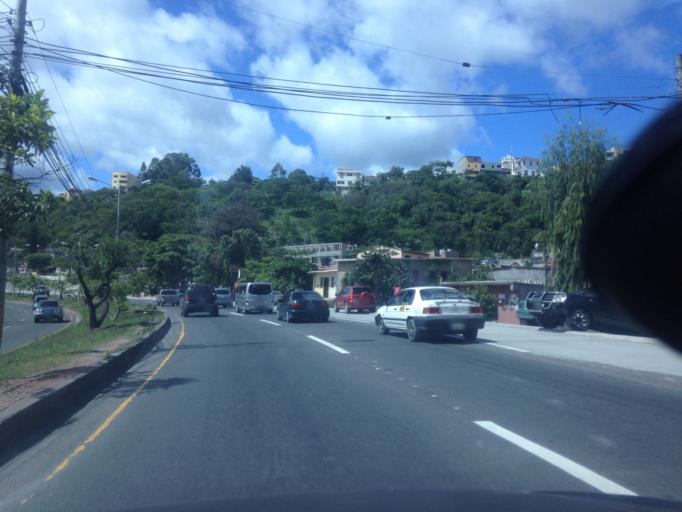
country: HN
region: Francisco Morazan
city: El Tablon
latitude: 14.0706
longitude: -87.1664
